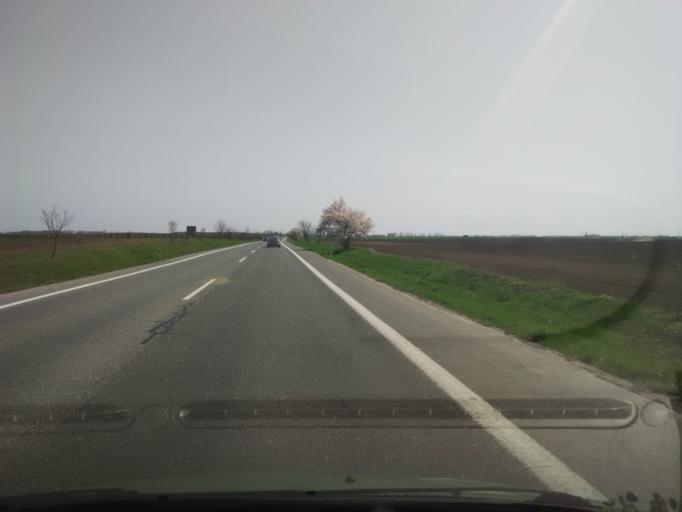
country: SK
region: Nitriansky
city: Surany
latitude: 48.1211
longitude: 18.0335
